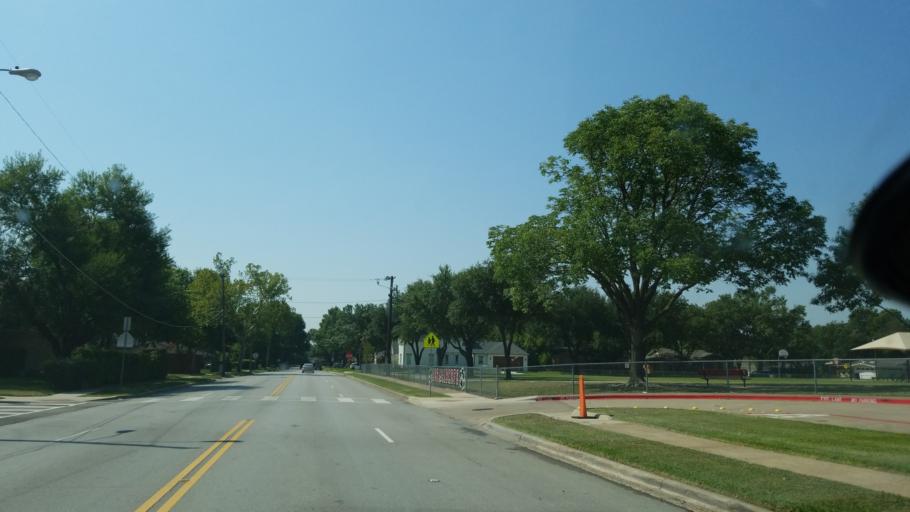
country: US
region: Texas
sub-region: Dallas County
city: Richardson
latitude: 32.8761
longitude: -96.7085
